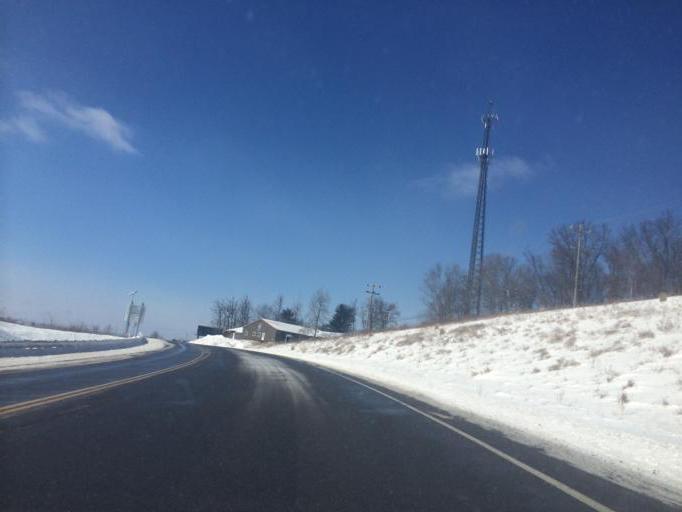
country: US
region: Pennsylvania
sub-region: Centre County
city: Park Forest Village
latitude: 40.8345
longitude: -77.9701
